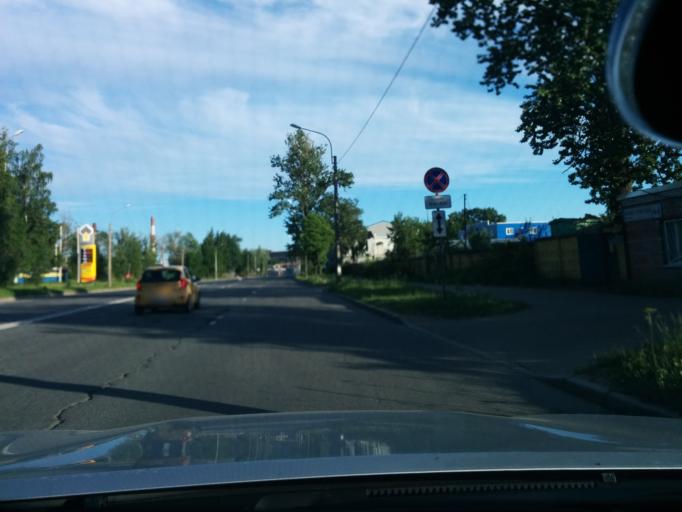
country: RU
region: Leningrad
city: Finlyandskiy
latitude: 59.9803
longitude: 30.3659
